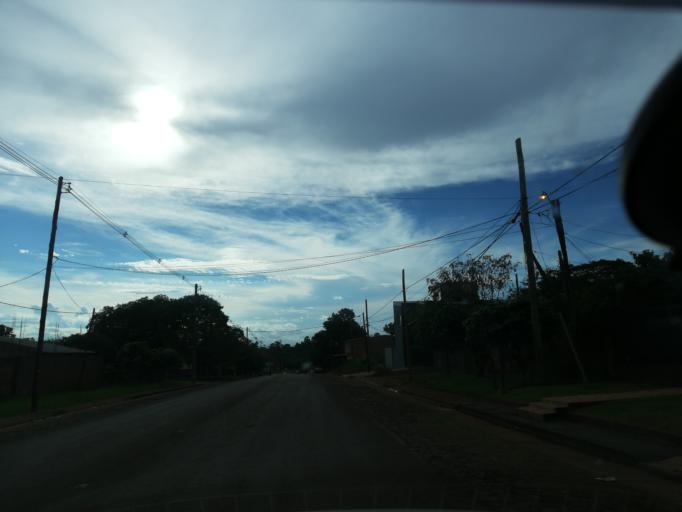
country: AR
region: Misiones
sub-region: Departamento de Capital
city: Posadas
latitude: -27.4190
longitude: -55.9281
